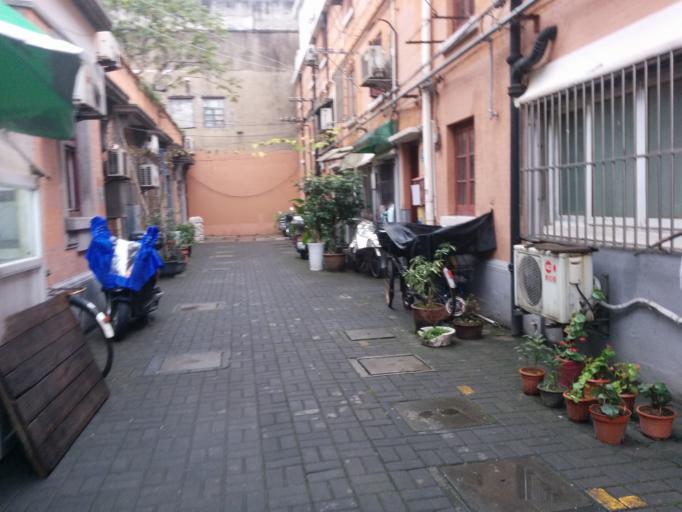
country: CN
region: Shanghai Shi
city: Shanghai
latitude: 31.2245
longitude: 121.4484
